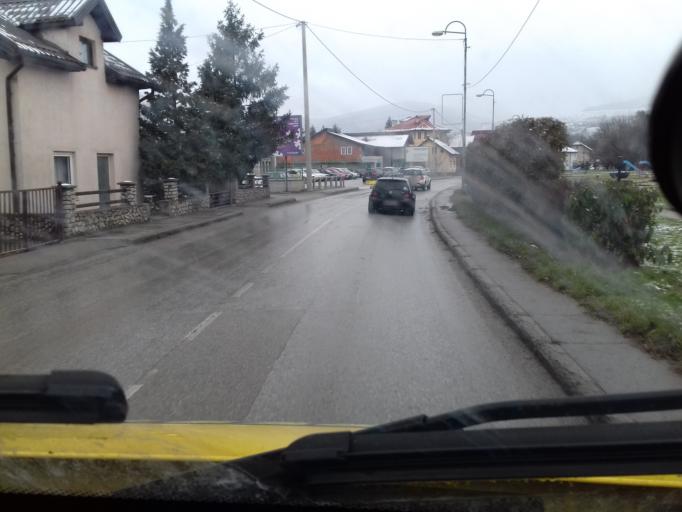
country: BA
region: Federation of Bosnia and Herzegovina
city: Kakanj
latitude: 44.1187
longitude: 18.1151
